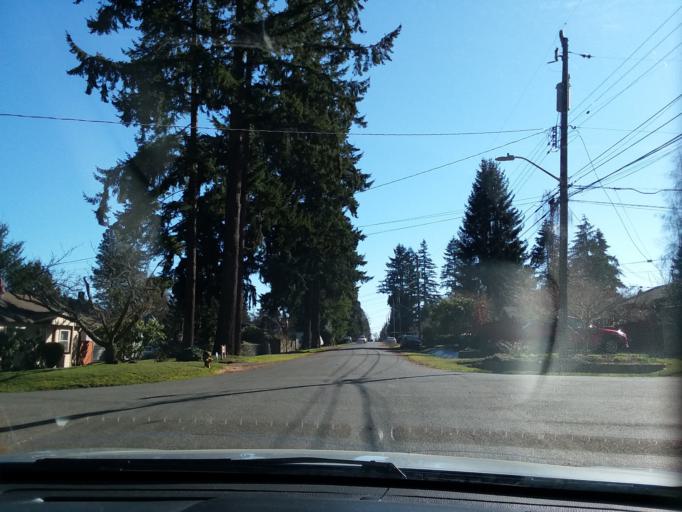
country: US
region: Washington
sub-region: King County
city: Shoreline
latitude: 47.7324
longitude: -122.3316
